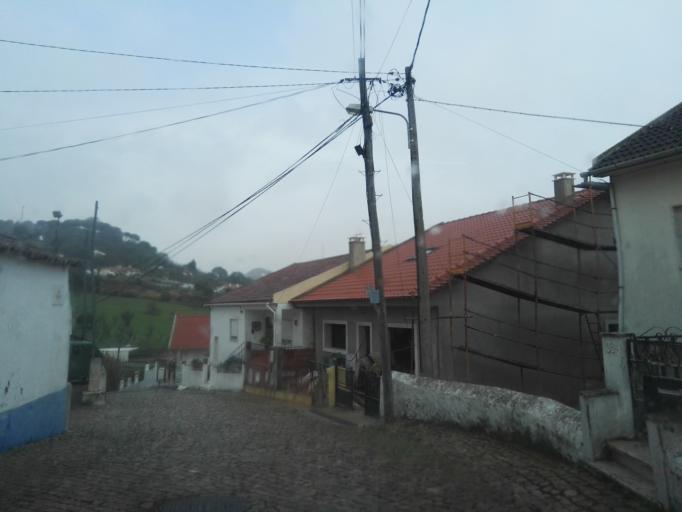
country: PT
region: Lisbon
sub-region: Vila Franca de Xira
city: Sobralinho
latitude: 38.9297
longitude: -9.0641
